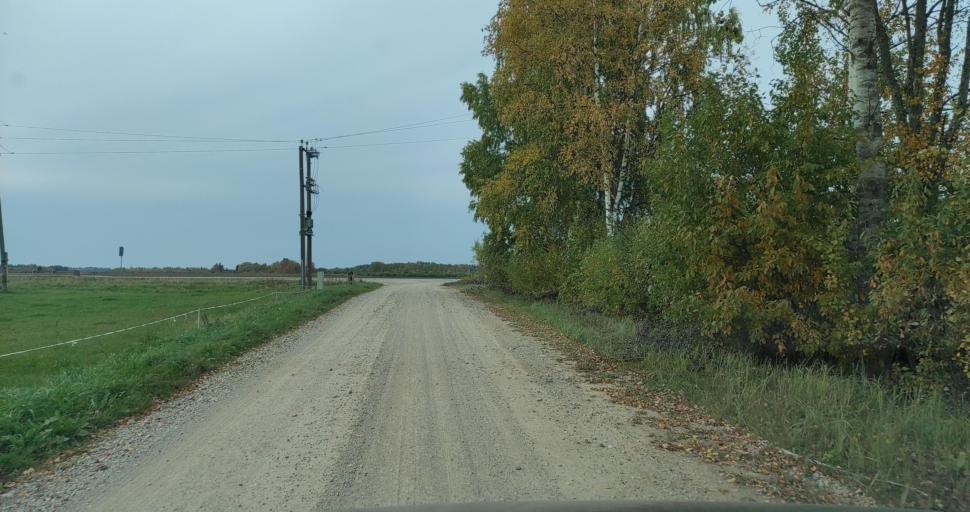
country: LV
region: Kuldigas Rajons
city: Kuldiga
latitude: 57.0288
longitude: 22.1963
